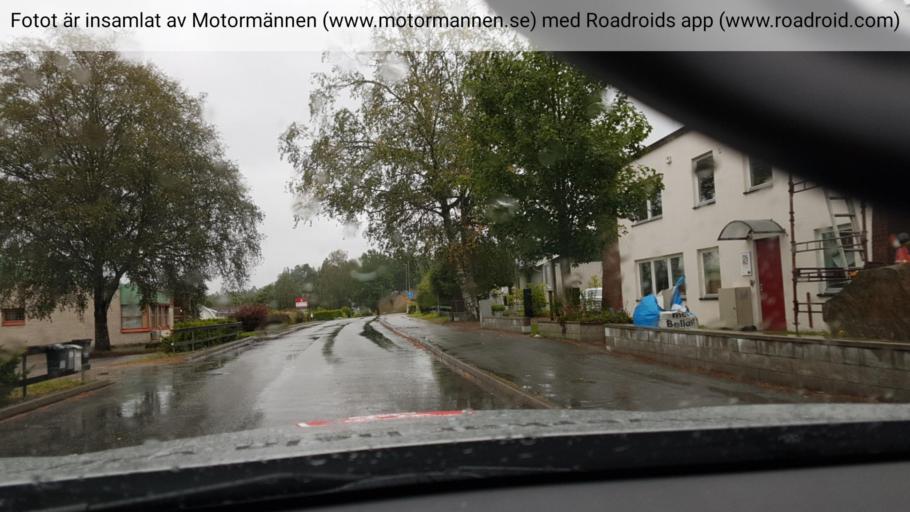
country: SE
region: Vaestra Goetaland
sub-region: Harryda Kommun
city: Hindas
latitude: 57.7040
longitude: 12.4436
